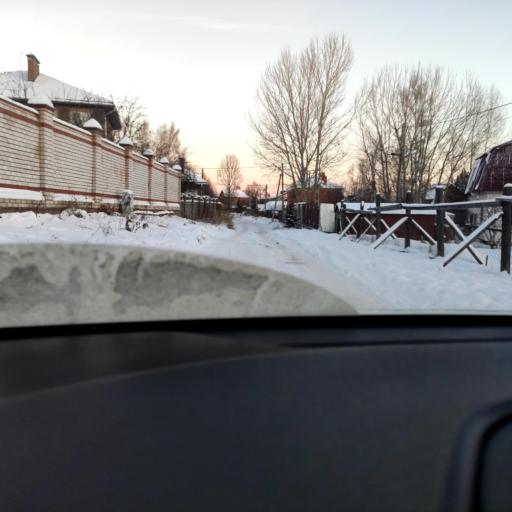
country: RU
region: Tatarstan
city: Stolbishchi
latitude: 55.7475
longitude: 49.2528
